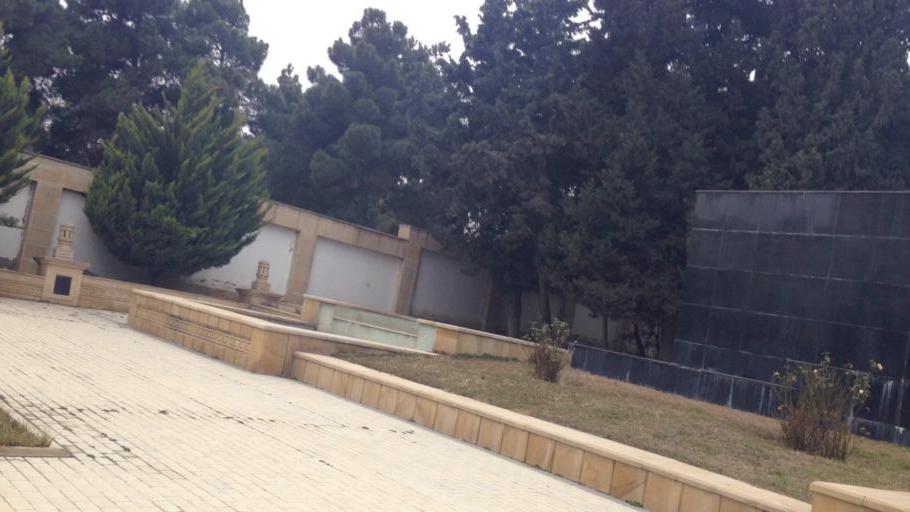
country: AZ
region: Baki
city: Badamdar
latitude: 40.3884
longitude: 49.8320
